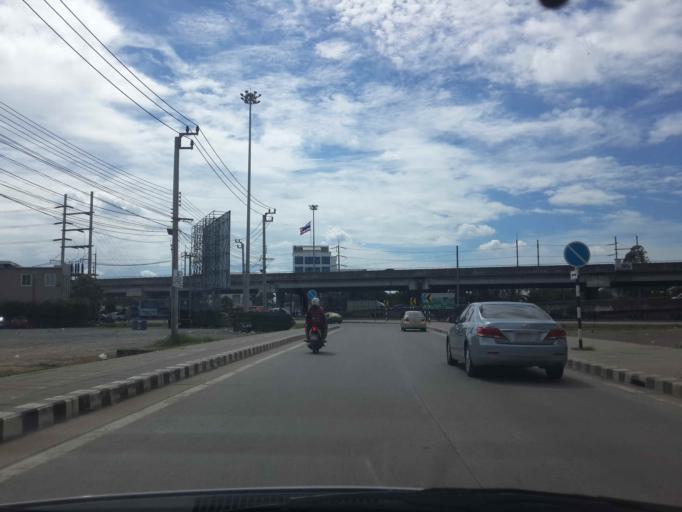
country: TH
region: Bangkok
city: Bang Khen
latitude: 13.8476
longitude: 100.6397
